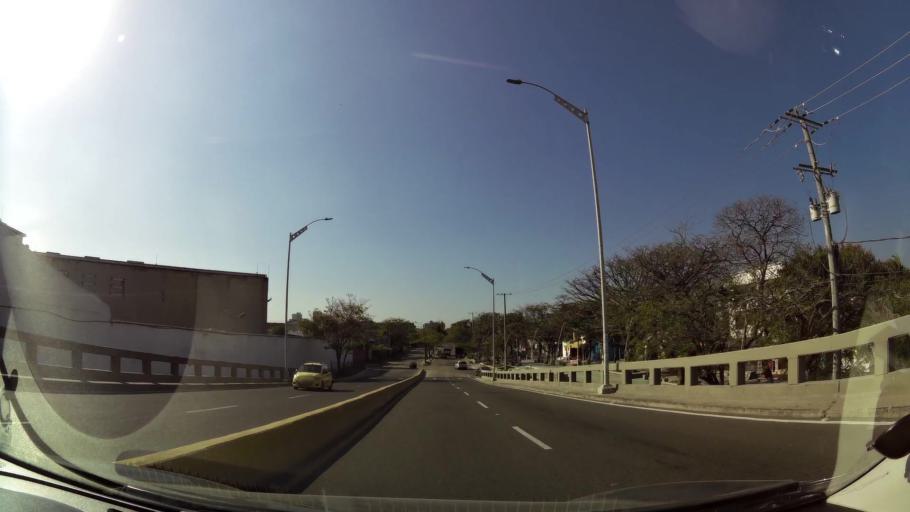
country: CO
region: Atlantico
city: Barranquilla
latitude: 10.9944
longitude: -74.7831
